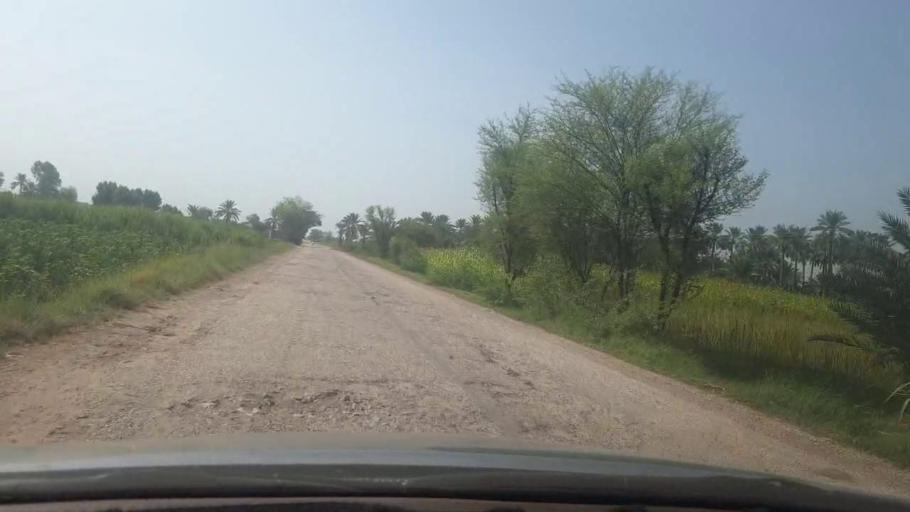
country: PK
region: Sindh
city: Gambat
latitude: 27.3160
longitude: 68.5589
